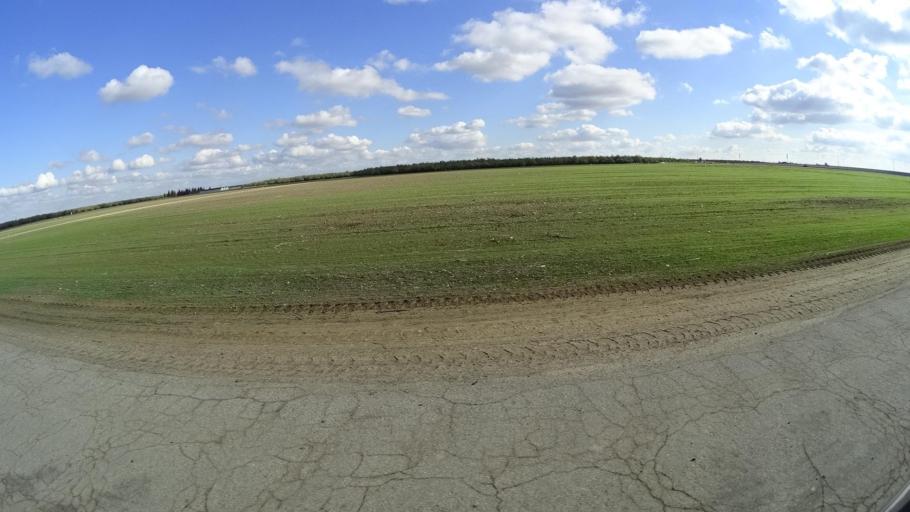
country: US
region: California
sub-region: Kern County
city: McFarland
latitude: 35.6774
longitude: -119.2683
